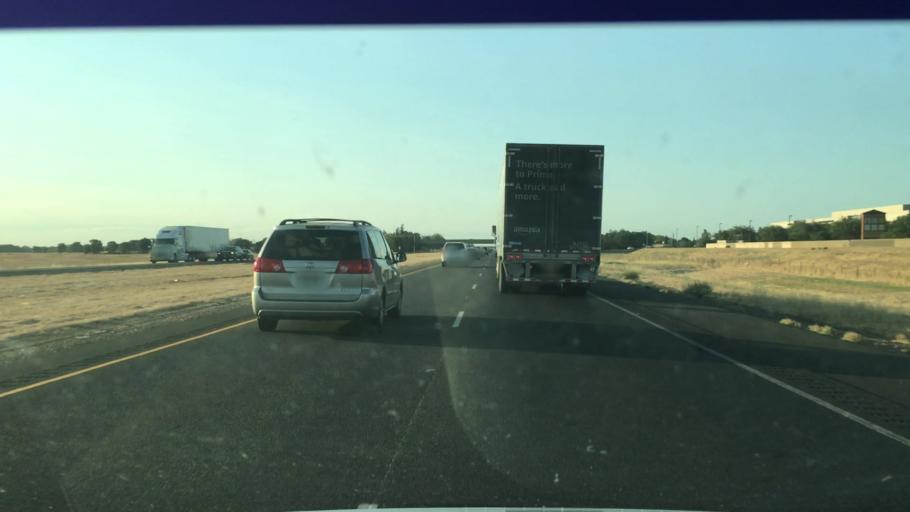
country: US
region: California
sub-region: Sacramento County
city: Laguna
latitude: 38.4033
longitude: -121.4824
